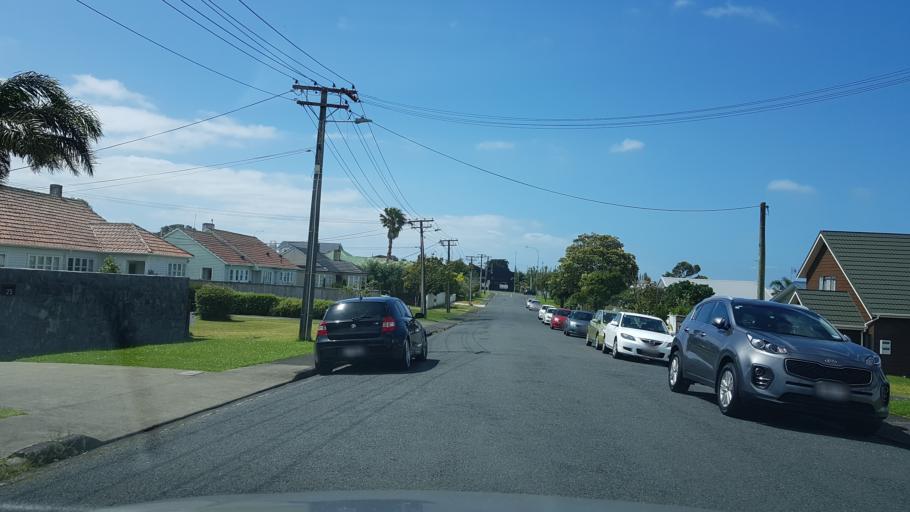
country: NZ
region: Auckland
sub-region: Auckland
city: North Shore
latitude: -36.8123
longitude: 174.7367
